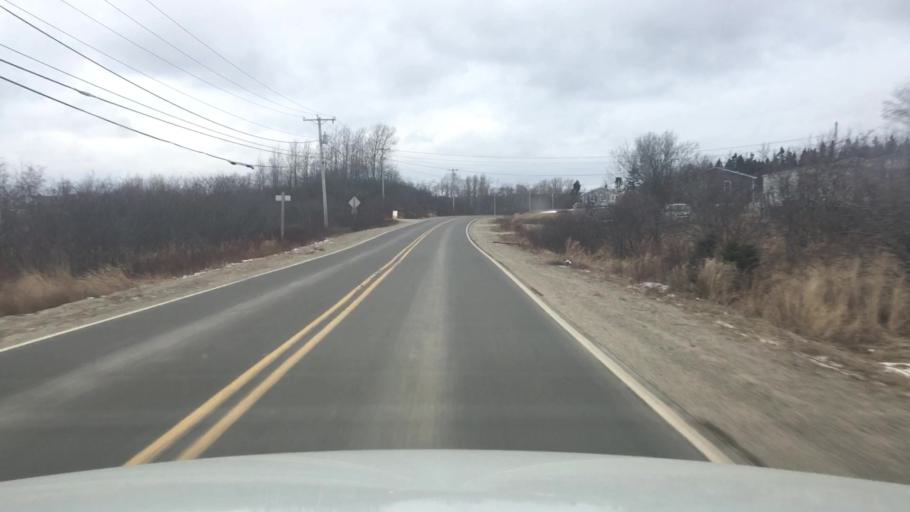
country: US
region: Maine
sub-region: Washington County
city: Jonesport
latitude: 44.5513
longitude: -67.6222
